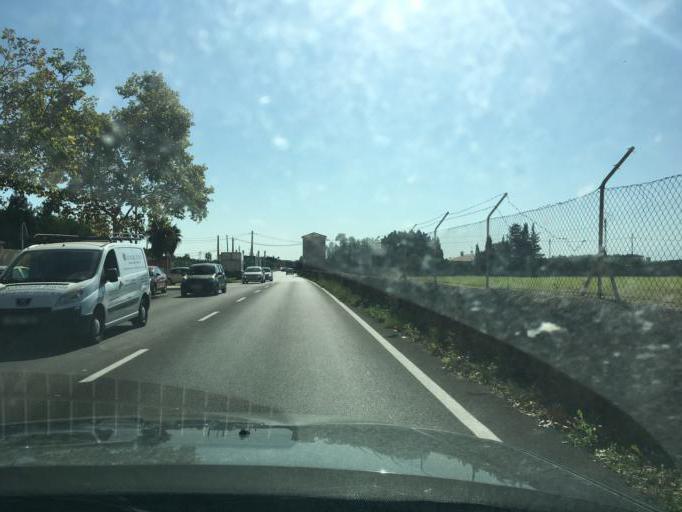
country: ES
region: Balearic Islands
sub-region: Illes Balears
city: Palma
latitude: 39.5817
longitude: 2.6830
